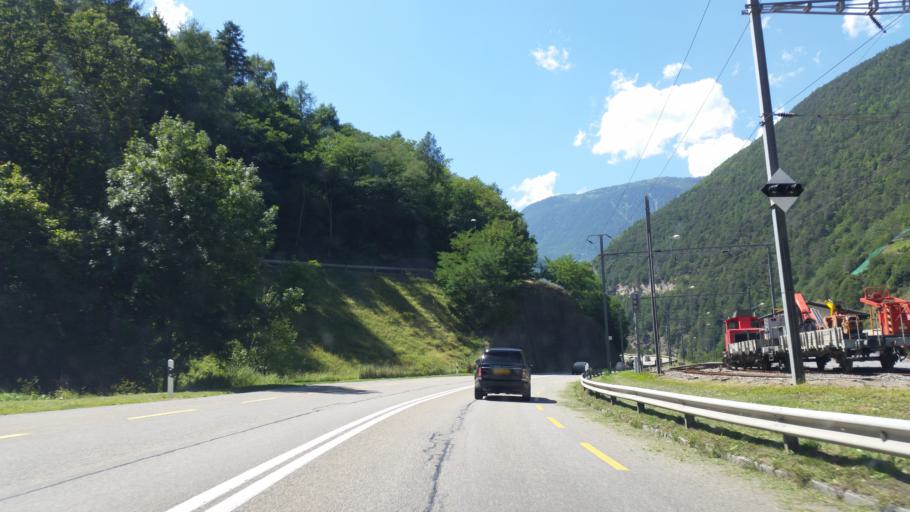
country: CH
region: Valais
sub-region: Martigny District
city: Martigny-Ville
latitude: 46.0786
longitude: 7.0840
